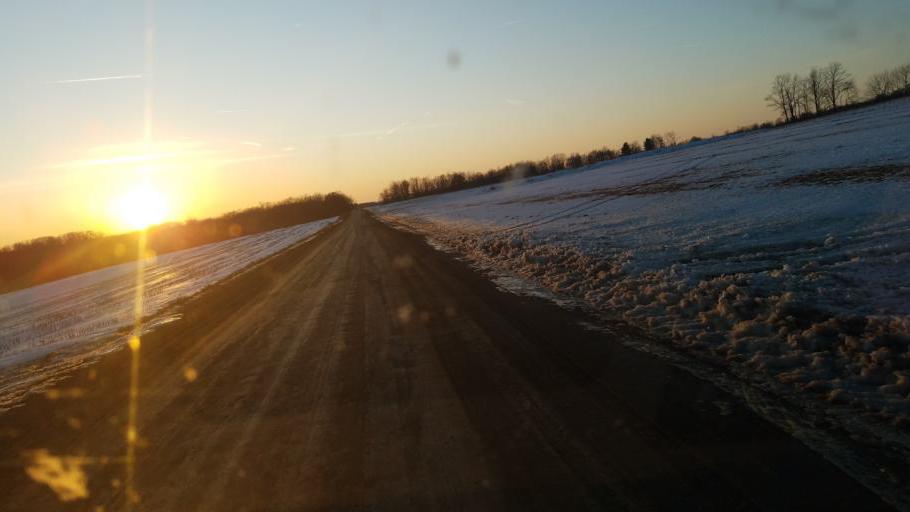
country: US
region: Pennsylvania
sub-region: Tioga County
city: Westfield
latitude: 42.0131
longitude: -77.6605
